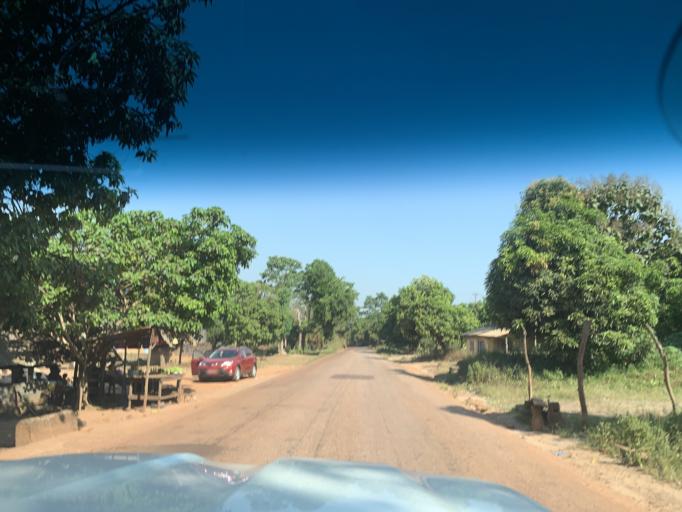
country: GN
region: Kindia
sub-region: Kindia
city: Kindia
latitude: 9.9136
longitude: -12.9962
